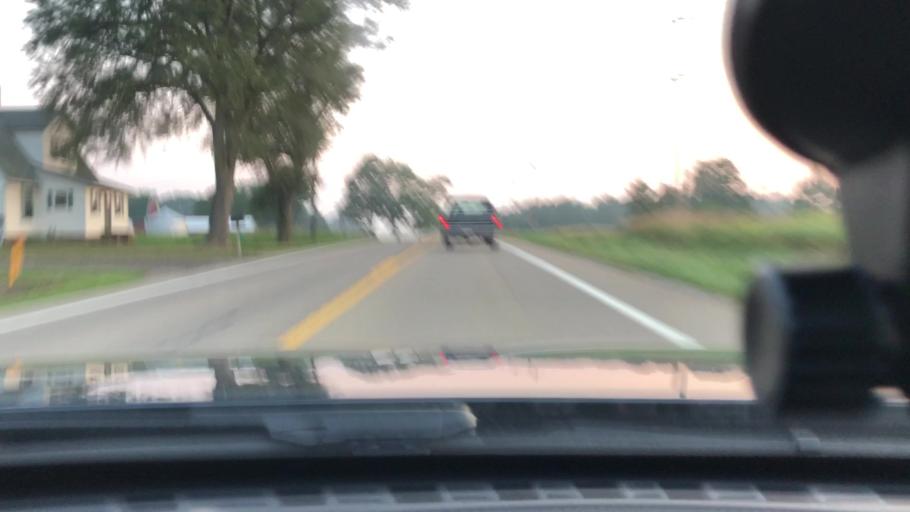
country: US
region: Michigan
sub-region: Washtenaw County
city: Chelsea
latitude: 42.2568
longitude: -84.0340
